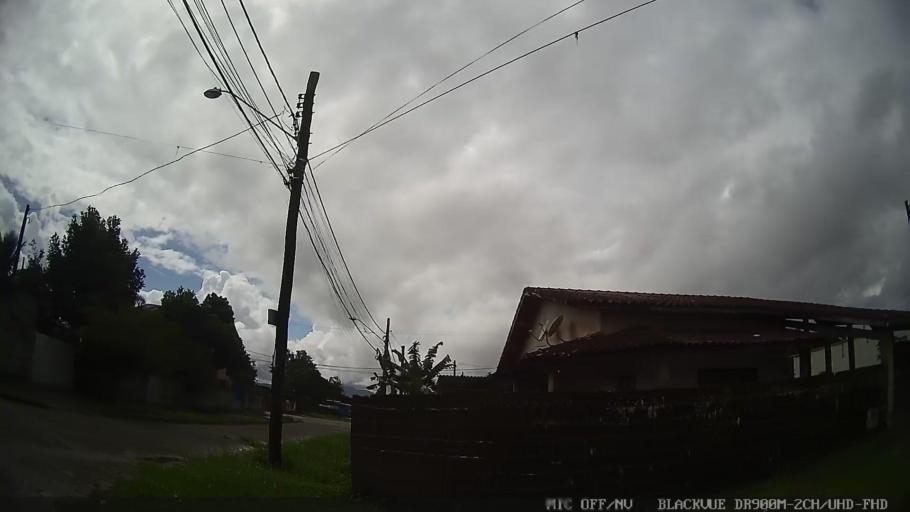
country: BR
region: Sao Paulo
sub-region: Itanhaem
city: Itanhaem
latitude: -24.1606
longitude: -46.7935
